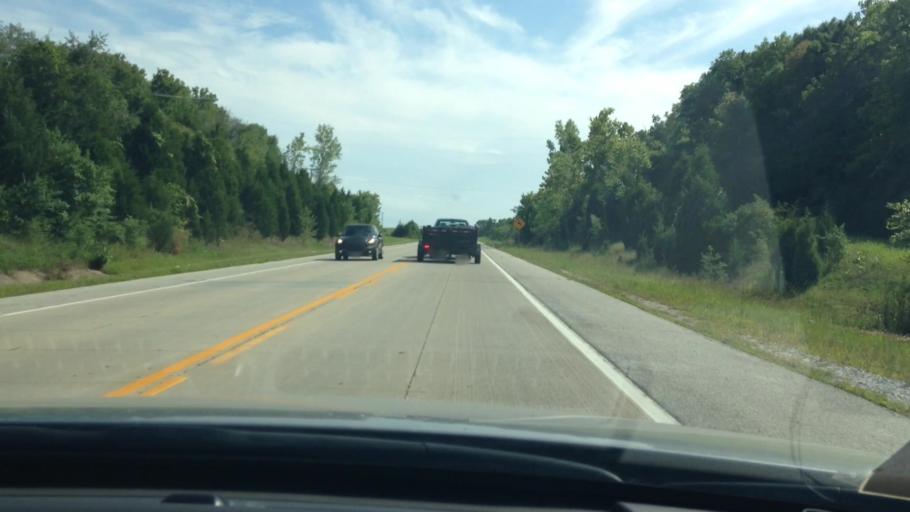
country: US
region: Missouri
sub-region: Jackson County
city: Grandview
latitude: 38.8582
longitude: -94.5858
